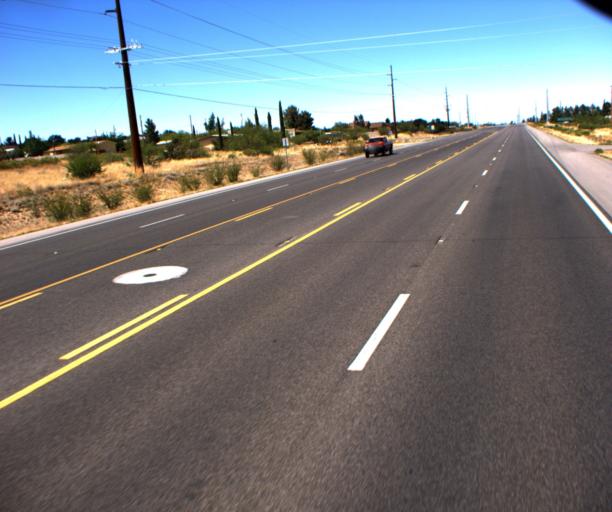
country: US
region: Arizona
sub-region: Cochise County
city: Sierra Vista Southeast
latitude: 31.4237
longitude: -110.2407
